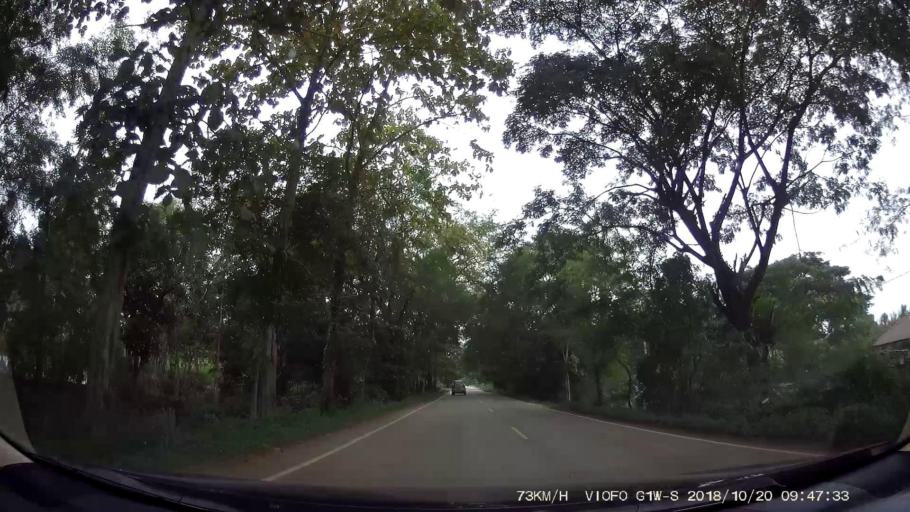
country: TH
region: Chaiyaphum
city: Khon San
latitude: 16.5046
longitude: 101.9186
